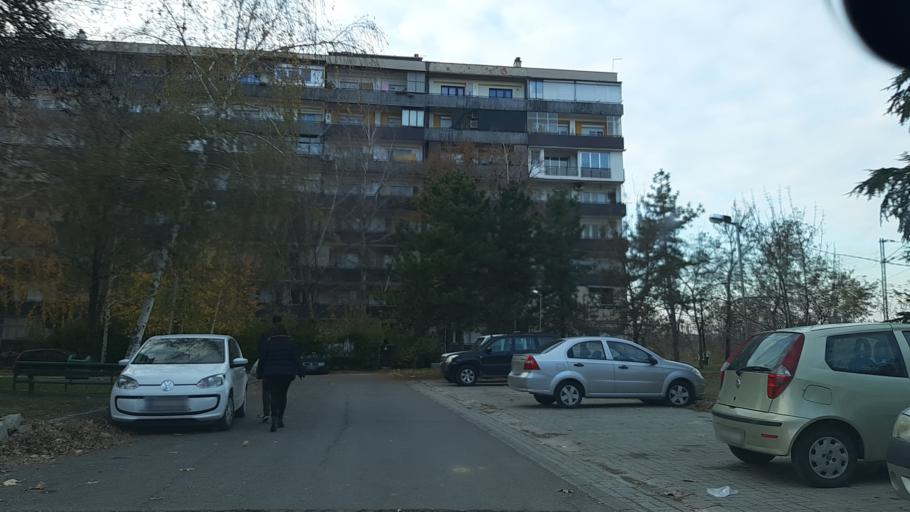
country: MK
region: Karpos
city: Skopje
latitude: 41.9817
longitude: 21.4453
